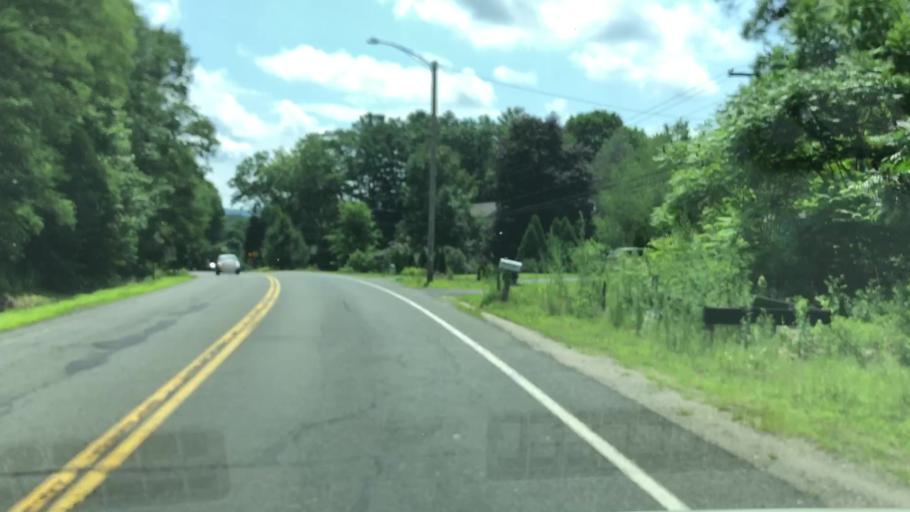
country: US
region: Massachusetts
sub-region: Hampshire County
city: Easthampton
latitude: 42.3036
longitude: -72.6751
